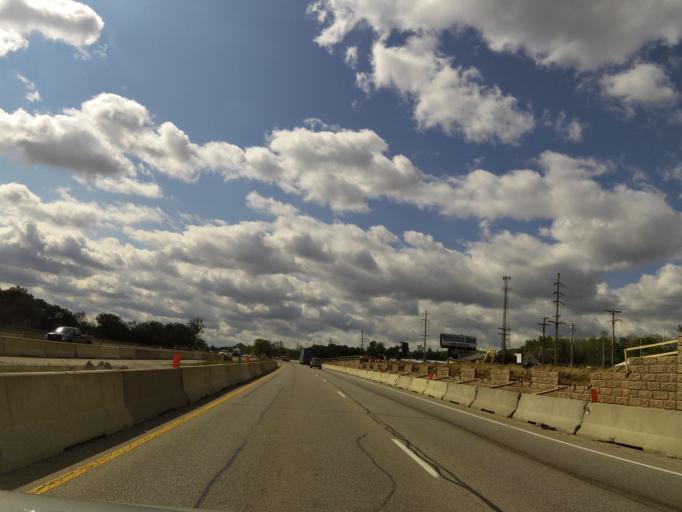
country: US
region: Ohio
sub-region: Fairfield County
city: Pickerington
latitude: 39.8056
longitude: -82.7119
